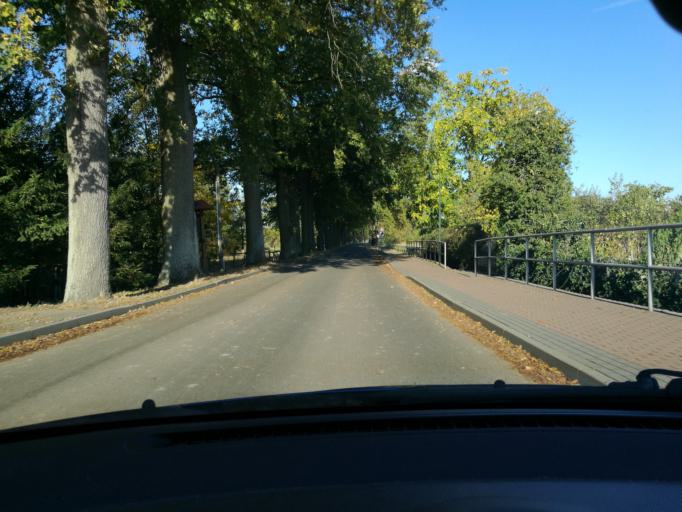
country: DE
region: Brandenburg
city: Lenzen
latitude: 53.1083
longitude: 11.4272
